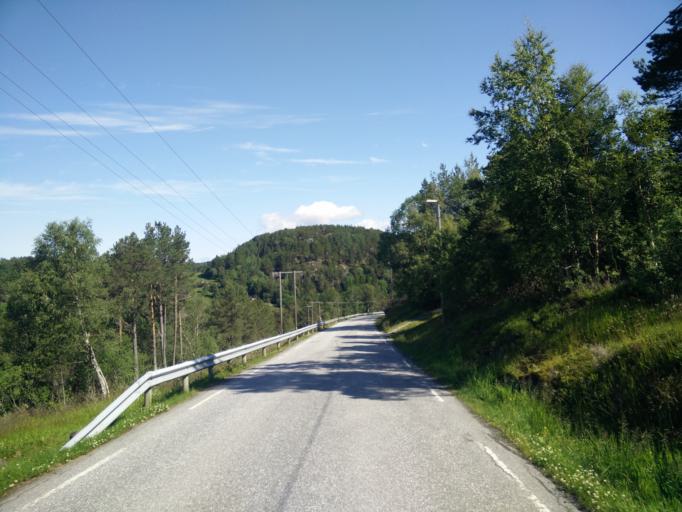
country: NO
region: More og Romsdal
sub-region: Kristiansund
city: Rensvik
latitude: 63.0668
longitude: 7.8703
